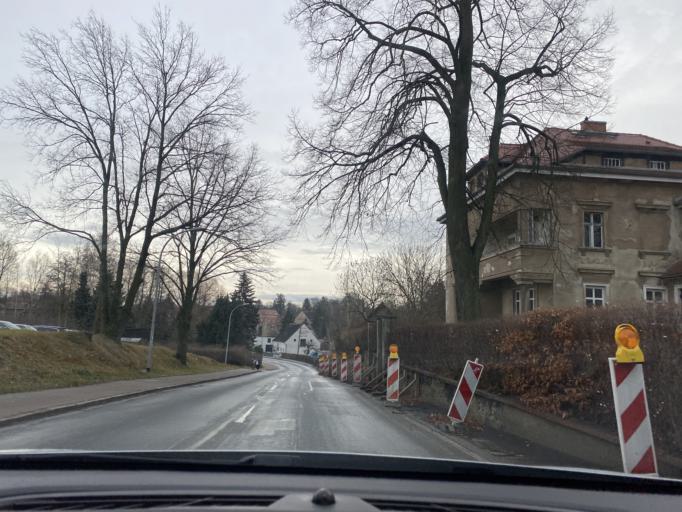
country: DE
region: Saxony
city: Reichenbach
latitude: 51.1425
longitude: 14.7967
